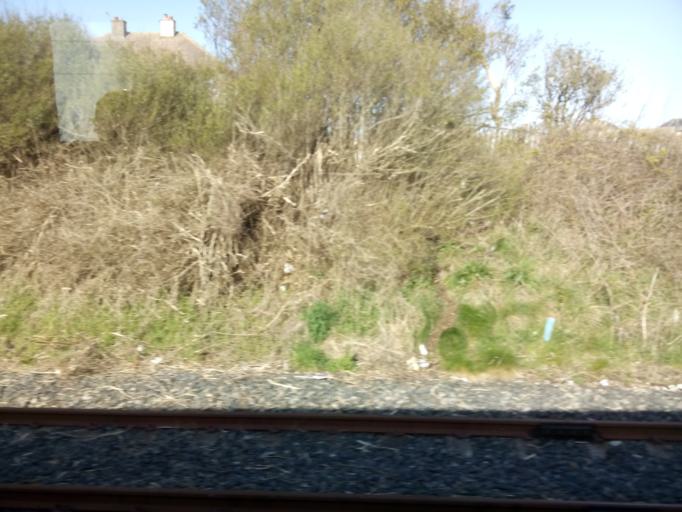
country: GB
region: England
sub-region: Northumberland
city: Berwick-Upon-Tweed
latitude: 55.7796
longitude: -2.0073
